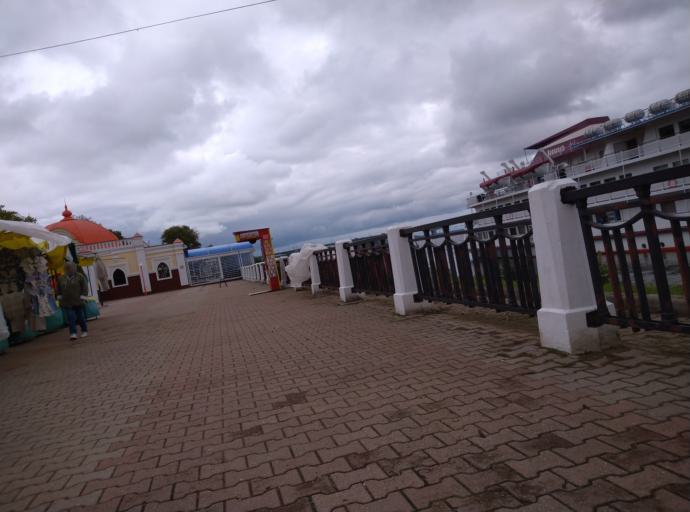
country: RU
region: Kostroma
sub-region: Kostromskoy Rayon
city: Kostroma
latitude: 57.7610
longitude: 40.9296
